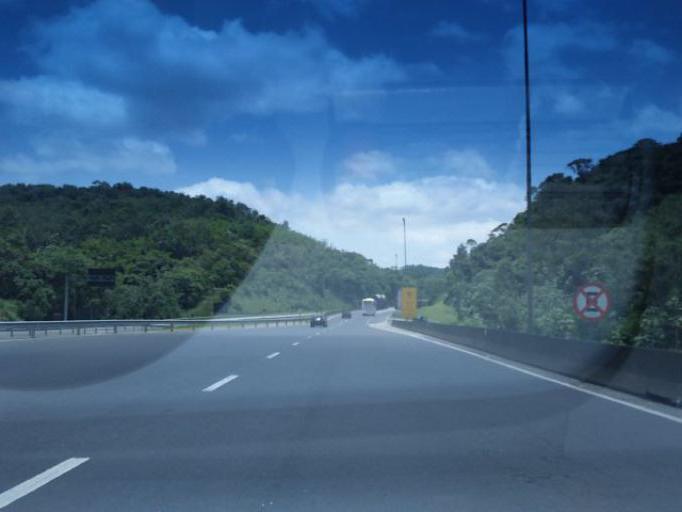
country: BR
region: Sao Paulo
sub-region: Juquia
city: Juquia
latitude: -24.3906
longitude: -47.7233
